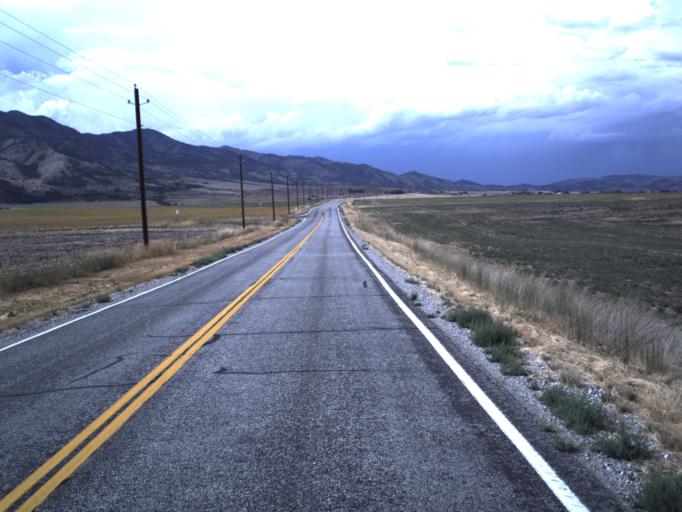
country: US
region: Utah
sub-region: Cache County
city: Benson
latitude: 41.8856
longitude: -112.0332
